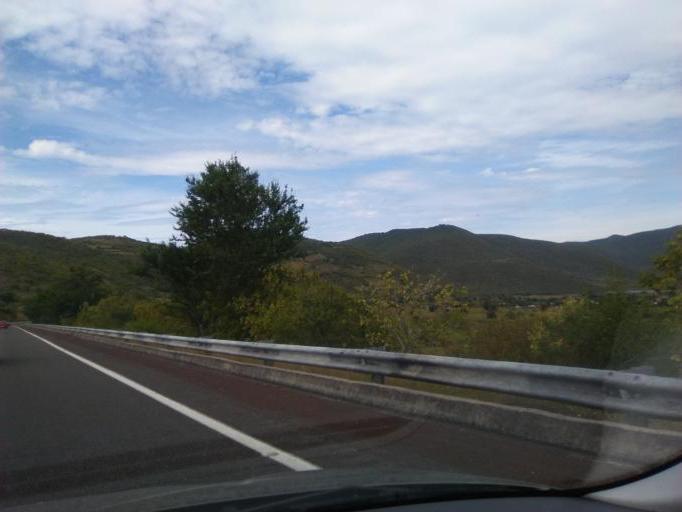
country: MX
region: Guerrero
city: Huitziltepec
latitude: 17.7495
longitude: -99.4893
